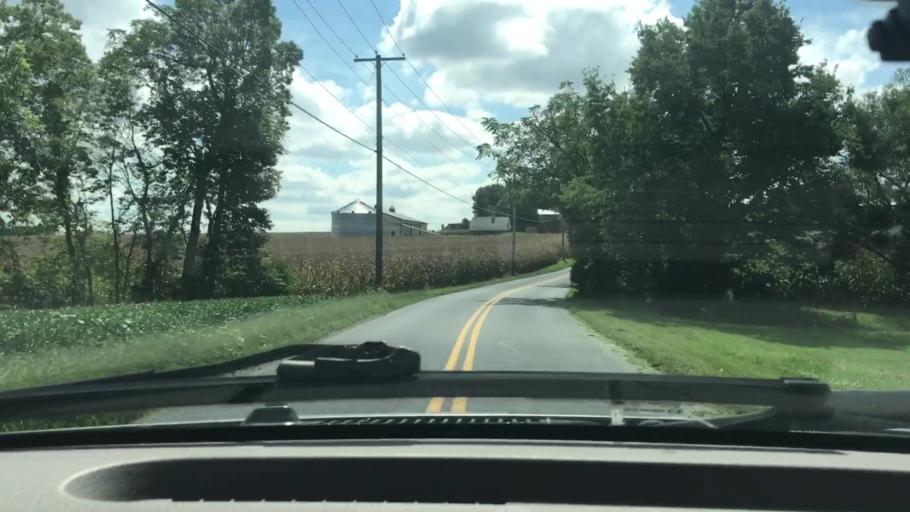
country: US
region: Pennsylvania
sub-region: Lancaster County
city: Landisville
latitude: 40.1075
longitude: -76.3865
